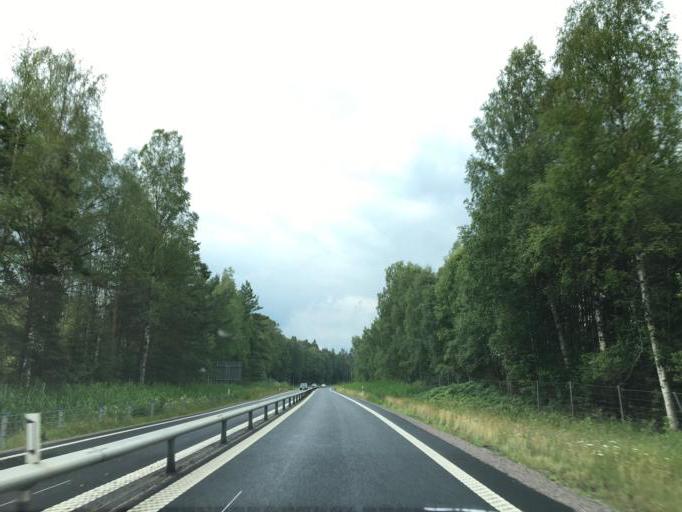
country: SE
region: Soedermanland
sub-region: Katrineholms Kommun
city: Katrineholm
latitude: 58.8814
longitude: 16.2018
